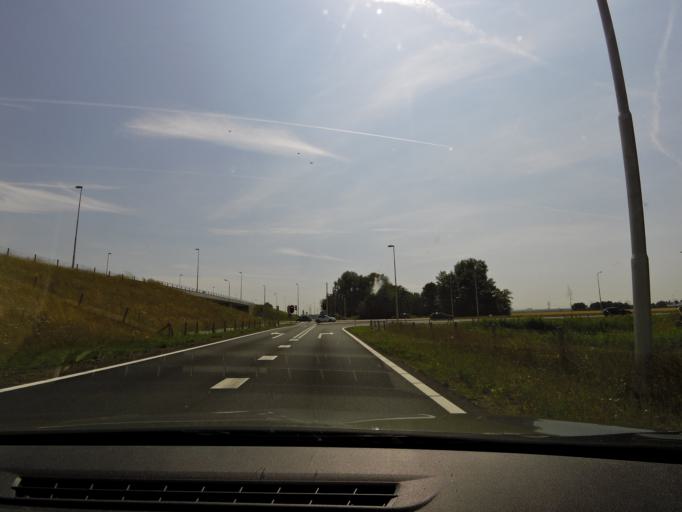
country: NL
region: South Holland
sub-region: Gemeente Brielle
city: Brielle
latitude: 51.8912
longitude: 4.1967
